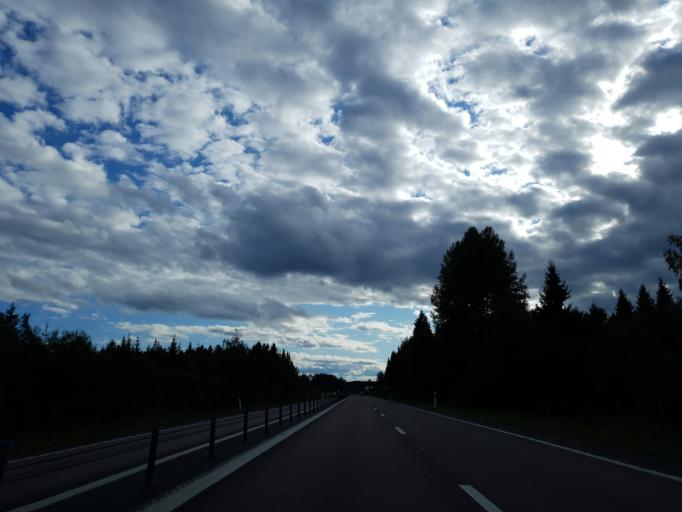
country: SE
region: Vaesternorrland
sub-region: Haernoesands Kommun
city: Haernoesand
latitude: 62.5953
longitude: 17.8028
